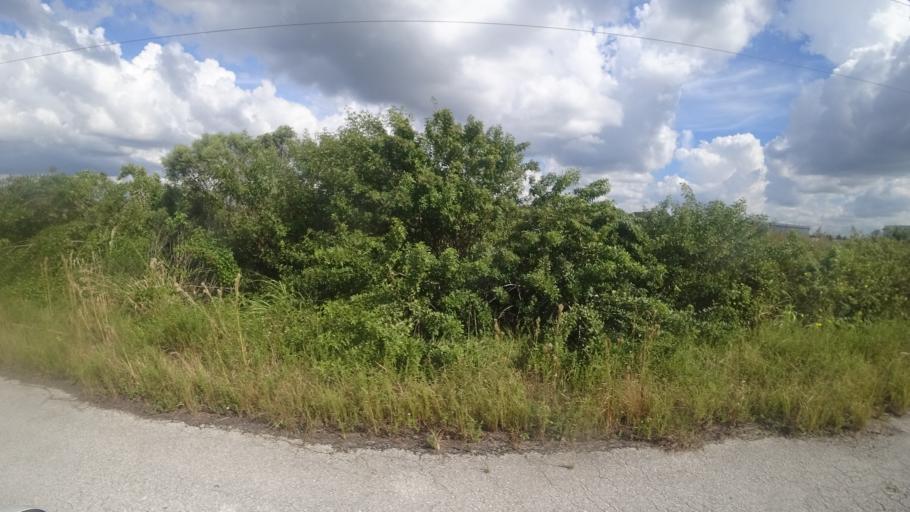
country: US
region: Florida
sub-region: Manatee County
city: Memphis
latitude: 27.6292
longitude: -82.5482
